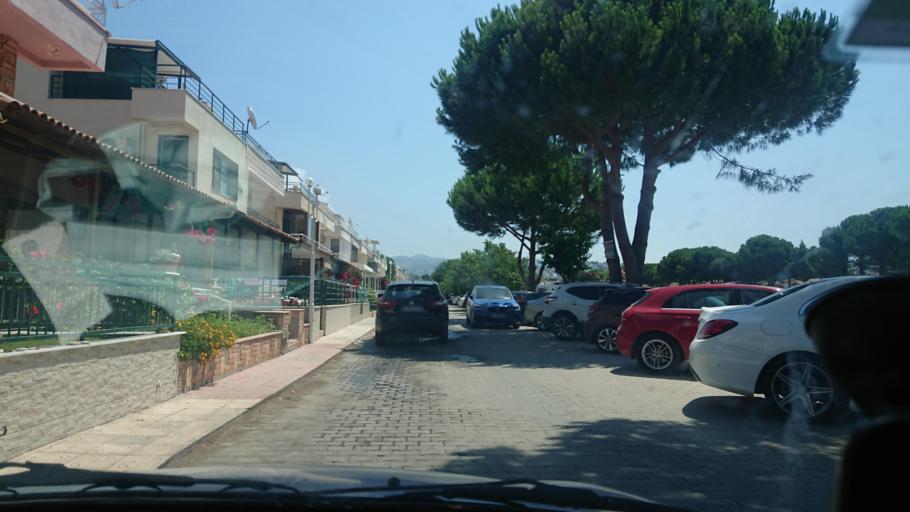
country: TR
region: Aydin
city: Kusadasi
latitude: 37.7982
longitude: 27.2706
